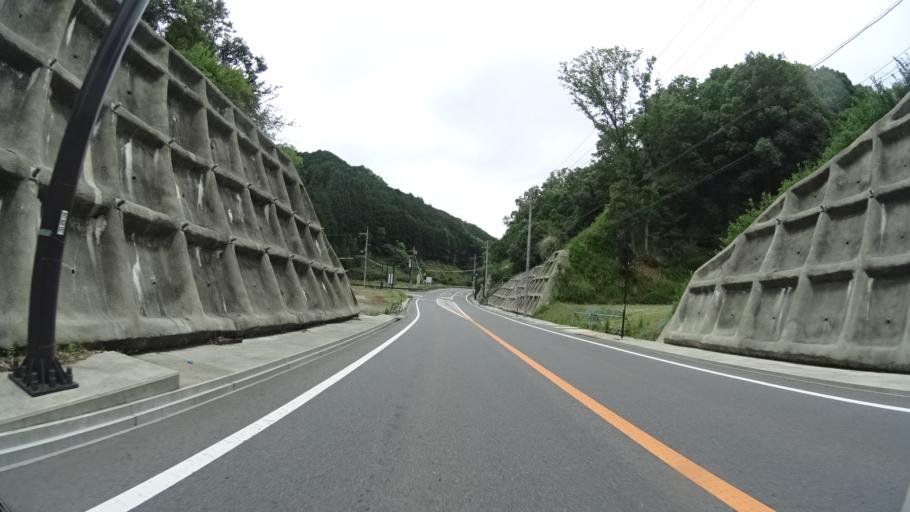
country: JP
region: Mie
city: Ueno-ebisumachi
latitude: 34.7696
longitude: 135.9793
